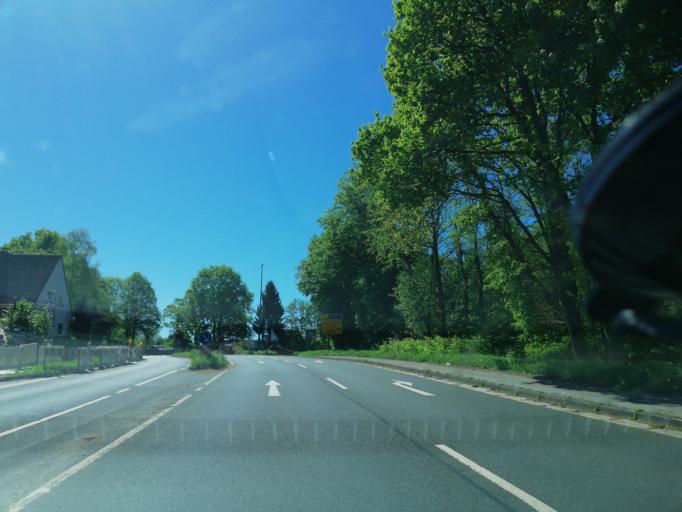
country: DE
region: North Rhine-Westphalia
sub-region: Regierungsbezirk Dusseldorf
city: Wuppertal
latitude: 51.2406
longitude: 7.2330
